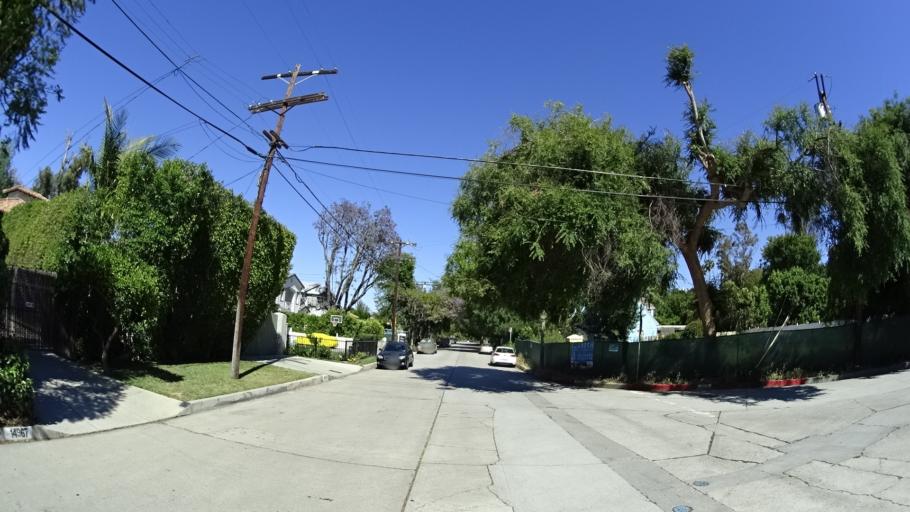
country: US
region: California
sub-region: Los Angeles County
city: Sherman Oaks
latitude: 34.1488
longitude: -118.4601
